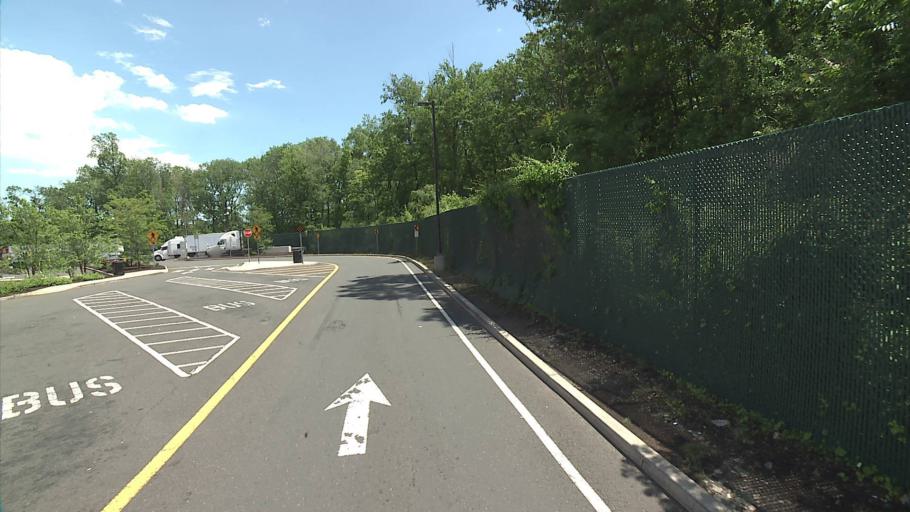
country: US
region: Connecticut
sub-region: New Haven County
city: Woodmont
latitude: 41.2452
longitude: -73.0092
